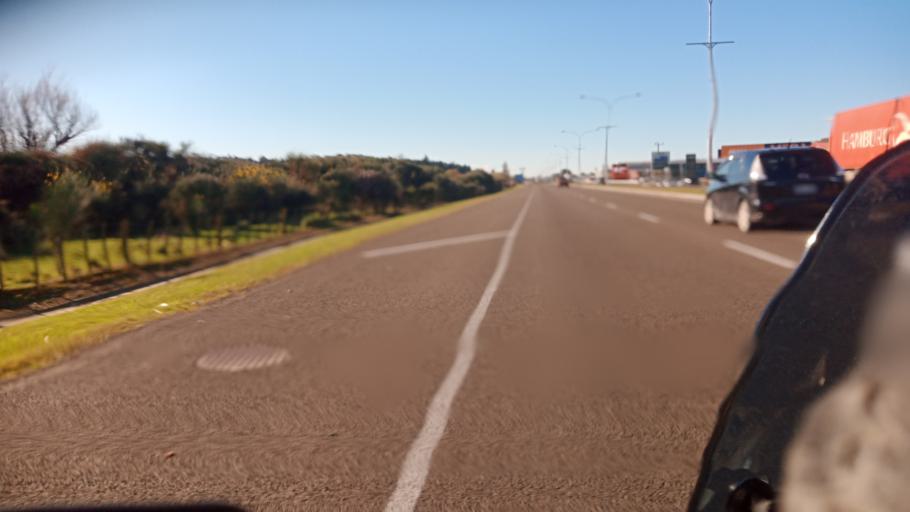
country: NZ
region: Hawke's Bay
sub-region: Napier City
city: Napier
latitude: -39.4963
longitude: 176.8807
